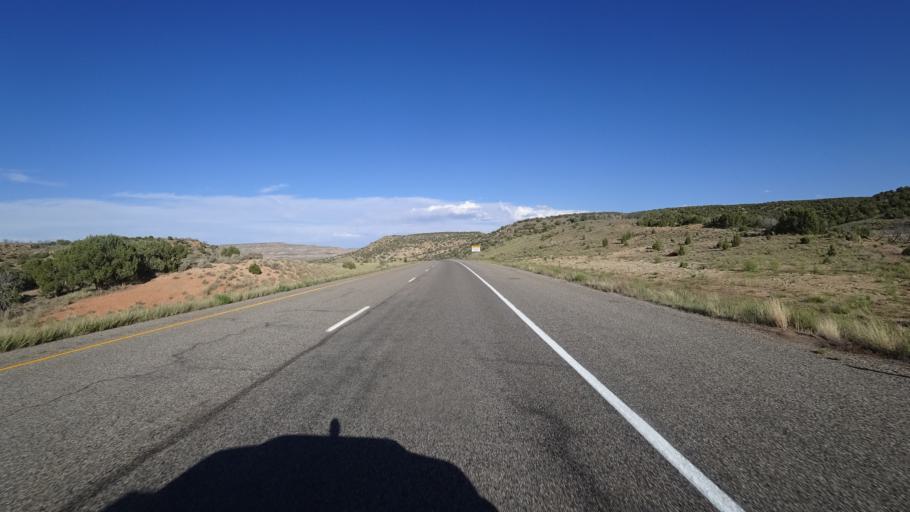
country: US
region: Colorado
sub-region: Mesa County
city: Loma
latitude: 39.1886
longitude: -109.0392
